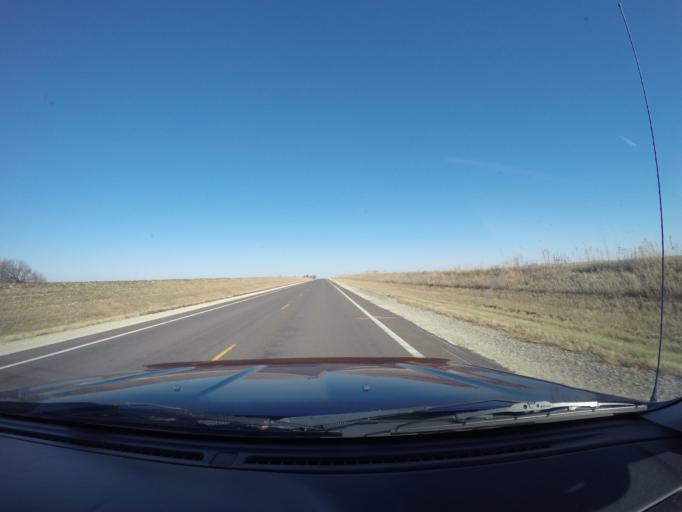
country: US
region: Kansas
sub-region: Marshall County
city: Blue Rapids
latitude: 39.6273
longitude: -96.7503
